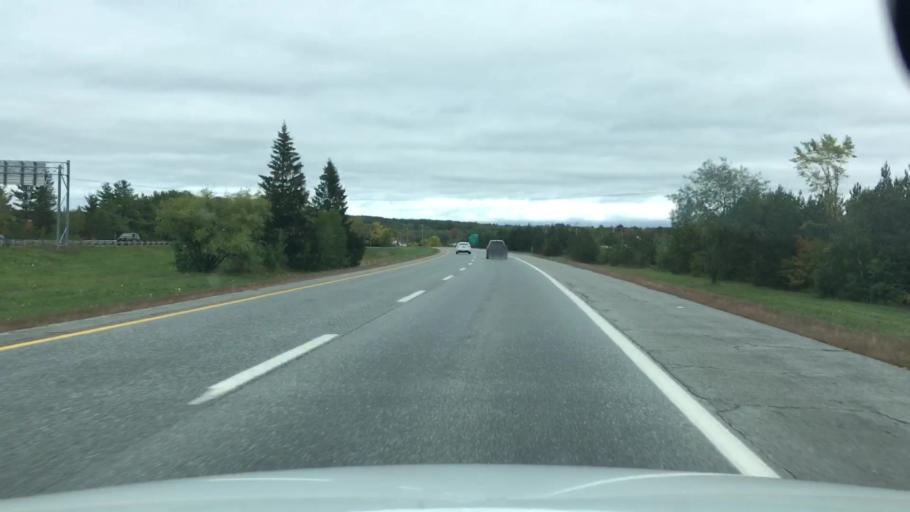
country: US
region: Maine
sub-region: Penobscot County
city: Brewer
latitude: 44.8269
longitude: -68.7499
